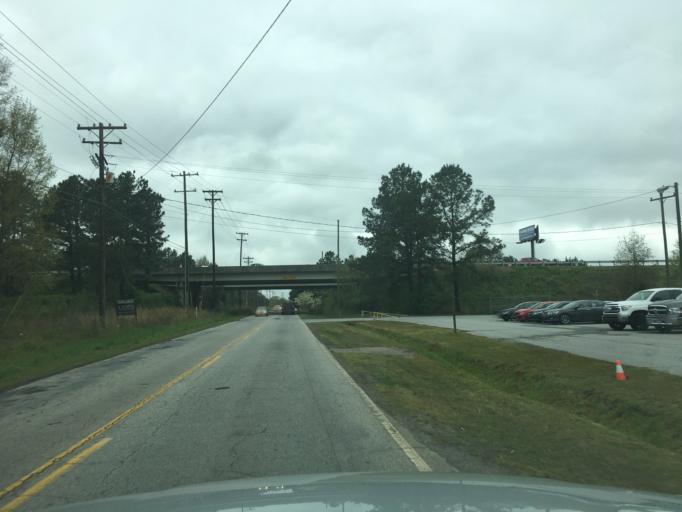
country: US
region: South Carolina
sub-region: Spartanburg County
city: Fairforest
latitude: 34.9670
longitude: -82.0276
